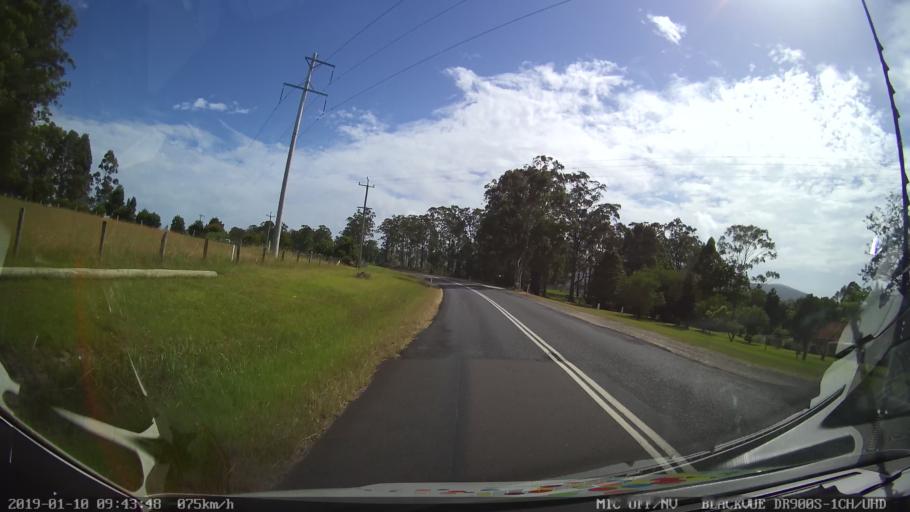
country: AU
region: New South Wales
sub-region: Coffs Harbour
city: Nana Glen
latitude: -30.1247
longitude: 153.0017
